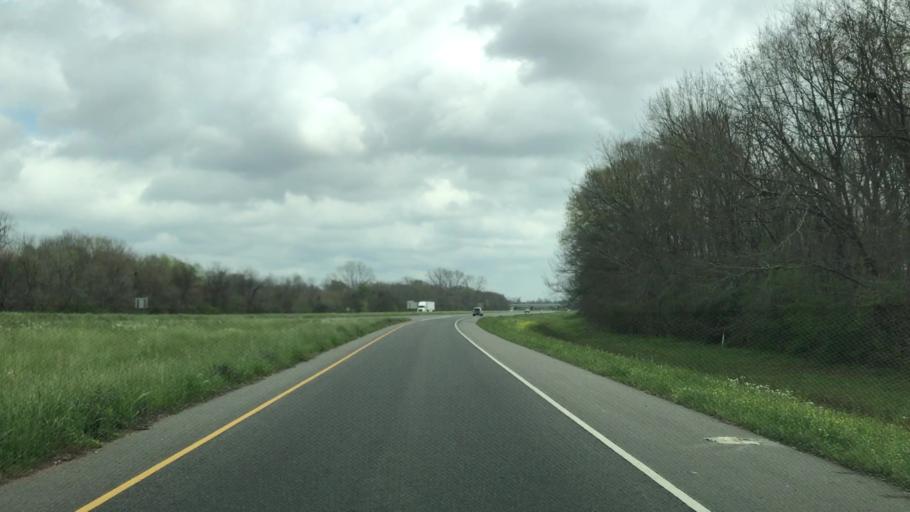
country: US
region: Louisiana
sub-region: Rapides Parish
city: Boyce
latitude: 31.3794
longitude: -92.6645
